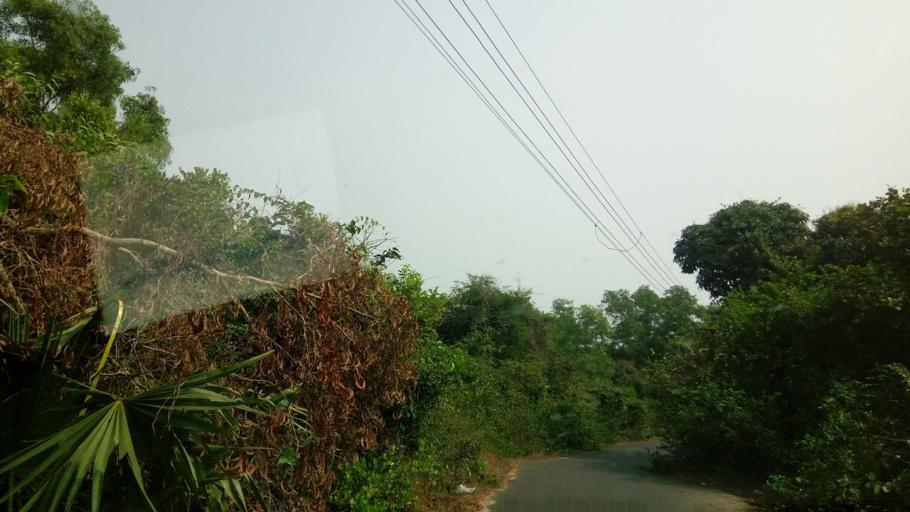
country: IN
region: Goa
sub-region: South Goa
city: Varca
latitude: 15.2192
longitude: 73.9345
